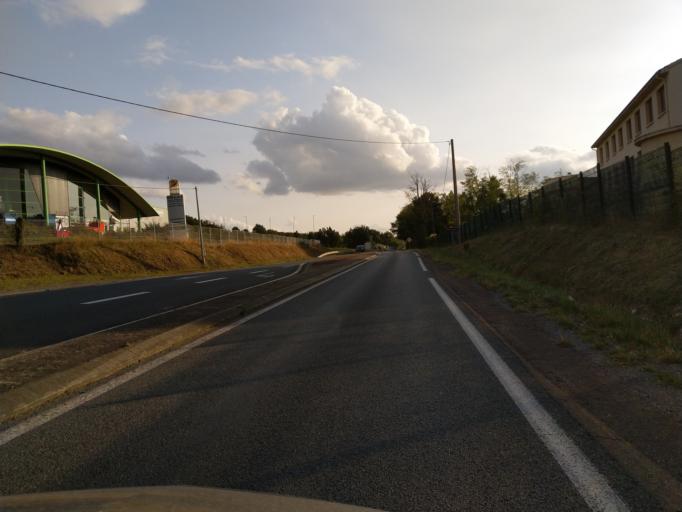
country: FR
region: Midi-Pyrenees
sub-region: Departement du Tarn
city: Realmont
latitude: 43.8281
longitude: 2.1903
